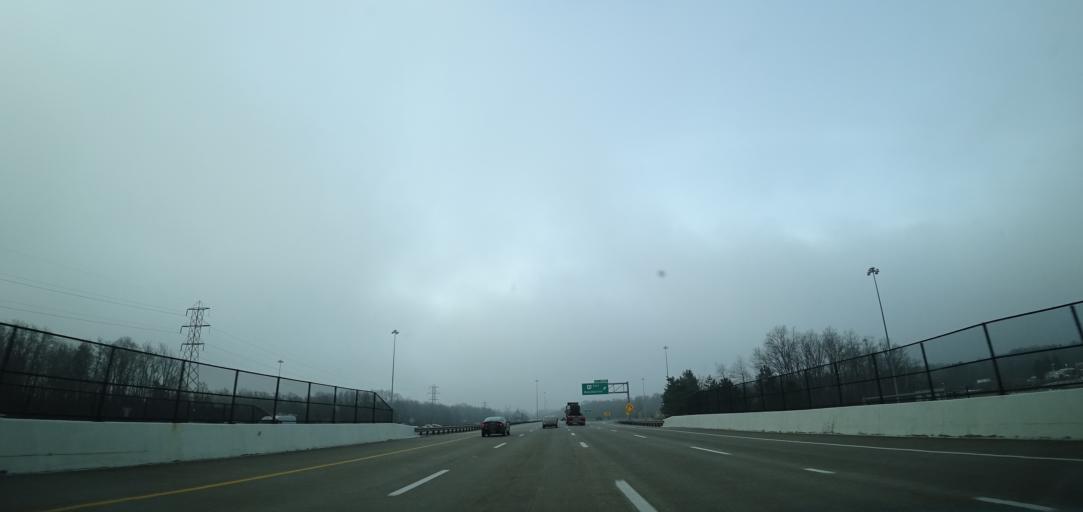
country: US
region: Ohio
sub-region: Cuyahoga County
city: Brecksville
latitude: 41.3167
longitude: -81.6491
